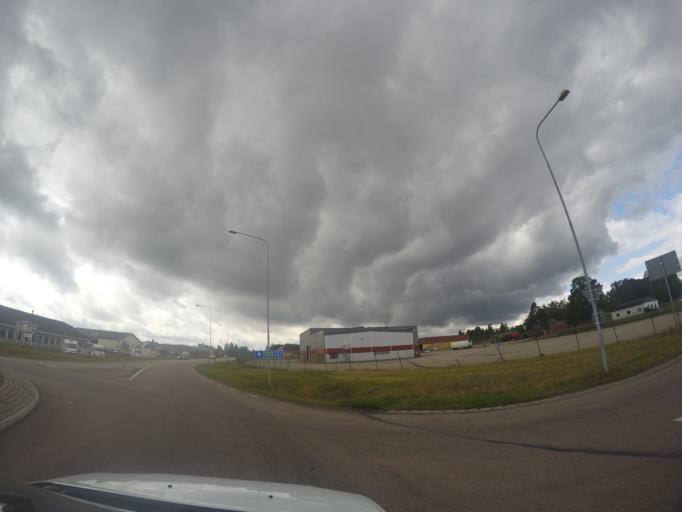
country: SE
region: Kronoberg
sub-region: Ljungby Kommun
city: Ljungby
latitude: 56.8179
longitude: 13.9172
